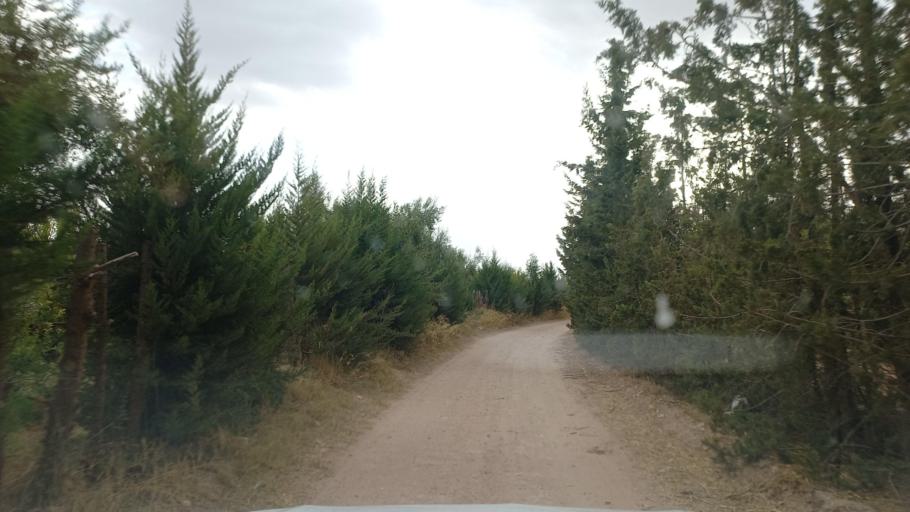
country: TN
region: Al Qasrayn
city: Sbiba
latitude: 35.2993
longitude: 9.0873
